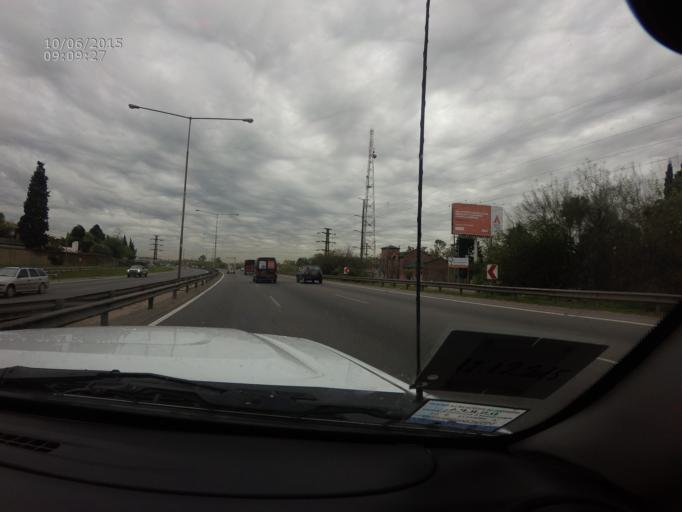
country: AR
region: Buenos Aires
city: Belen de Escobar
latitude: -34.3767
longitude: -58.7544
